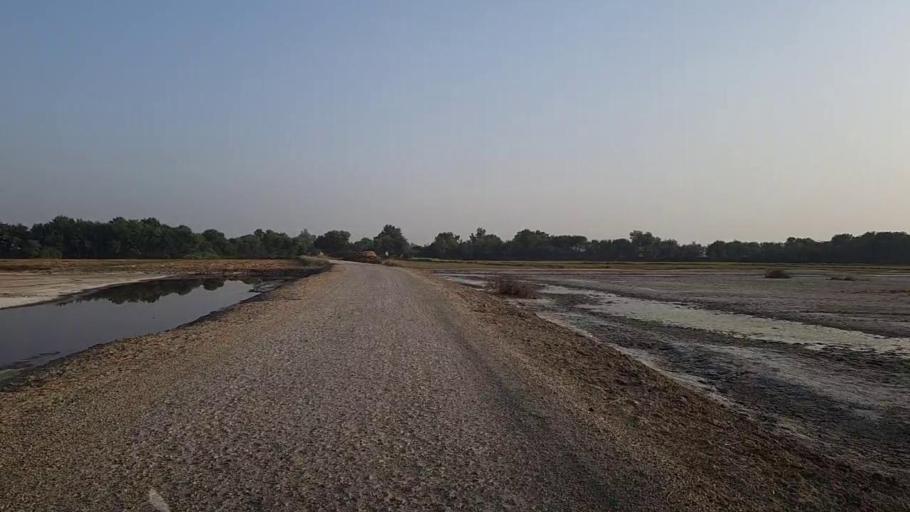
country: PK
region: Sindh
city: Kandhkot
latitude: 28.2433
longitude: 69.0916
